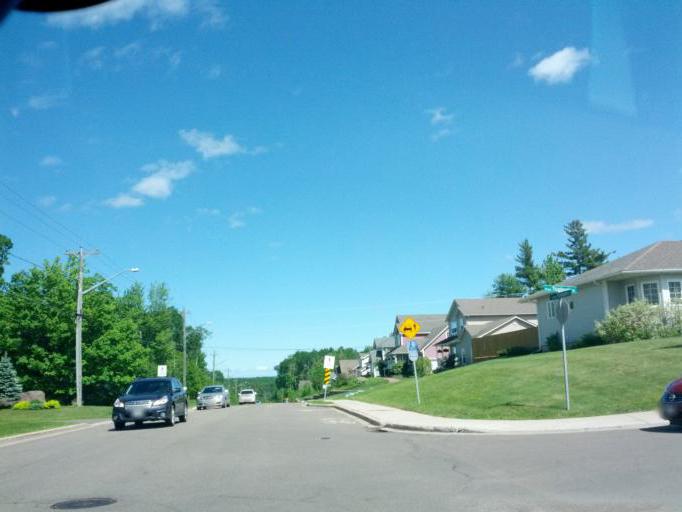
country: CA
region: New Brunswick
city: Moncton
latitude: 46.1221
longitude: -64.8379
